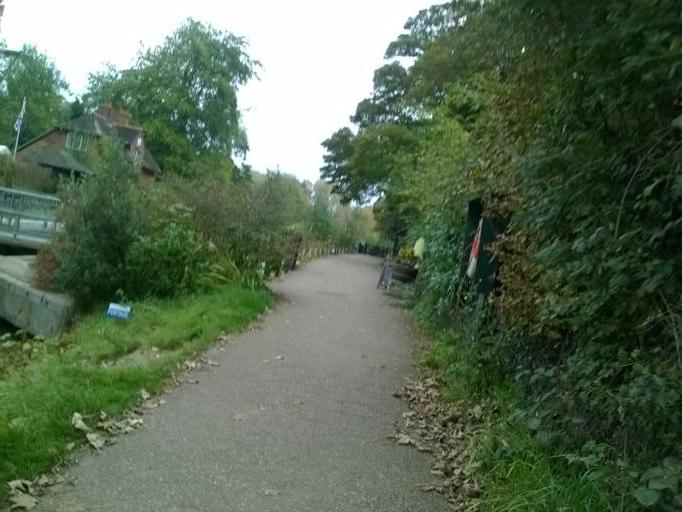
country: GB
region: England
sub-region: Wokingham
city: Sonning
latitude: 51.4726
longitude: -0.9184
